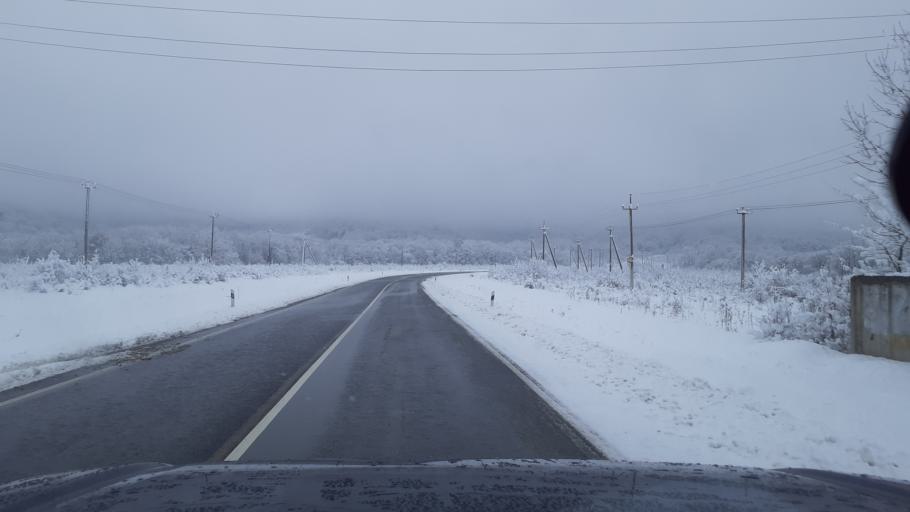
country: RU
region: Adygeya
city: Kamennomostskiy
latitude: 44.2165
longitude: 40.2037
